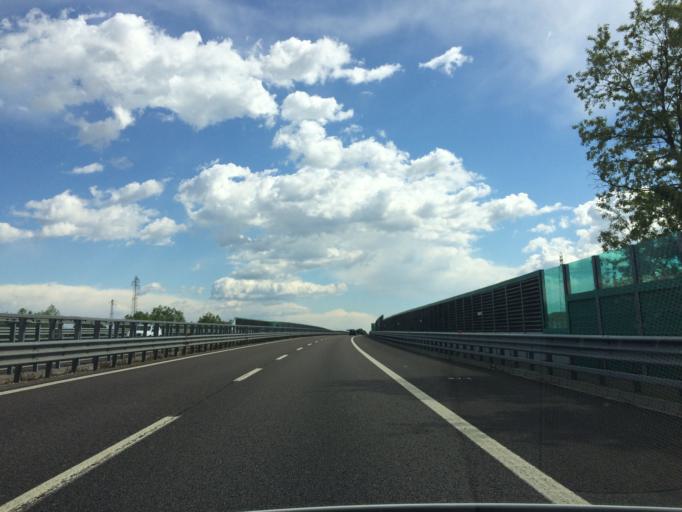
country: IT
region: Veneto
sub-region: Provincia di Vicenza
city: Marola
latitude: 45.5438
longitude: 11.6231
